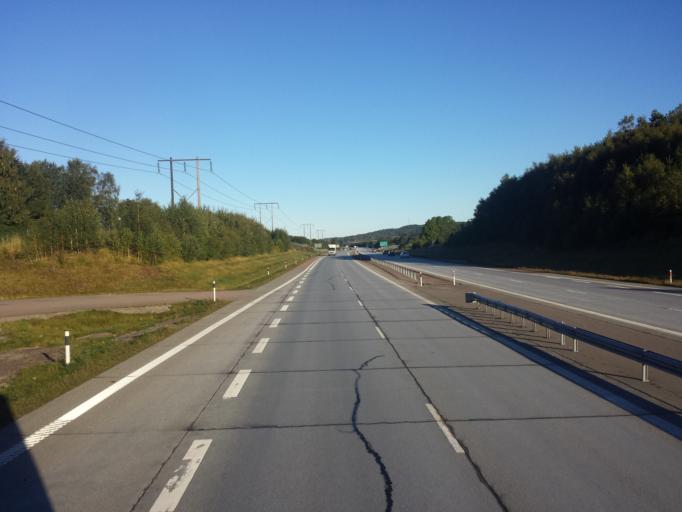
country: SE
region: Halland
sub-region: Halmstads Kommun
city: Getinge
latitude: 56.8541
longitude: 12.6729
